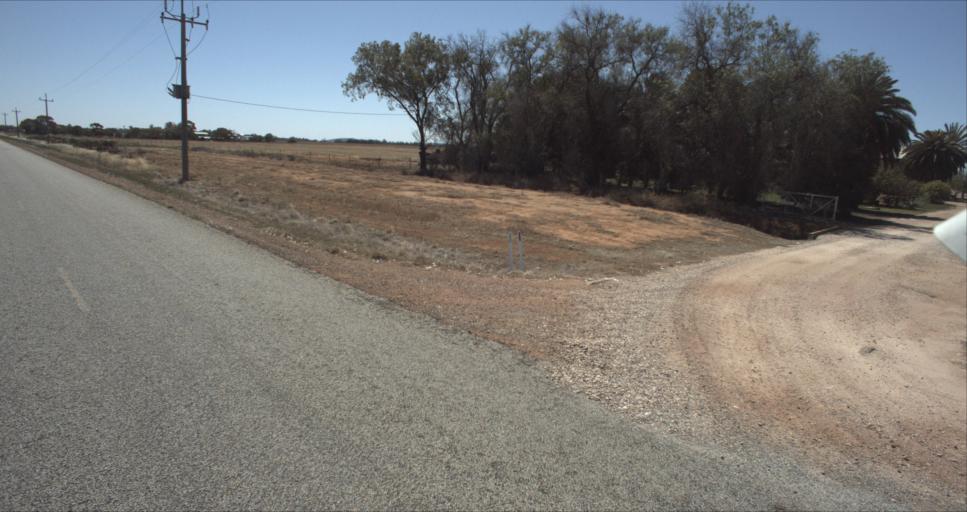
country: AU
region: New South Wales
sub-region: Leeton
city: Leeton
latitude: -34.4519
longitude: 146.2958
